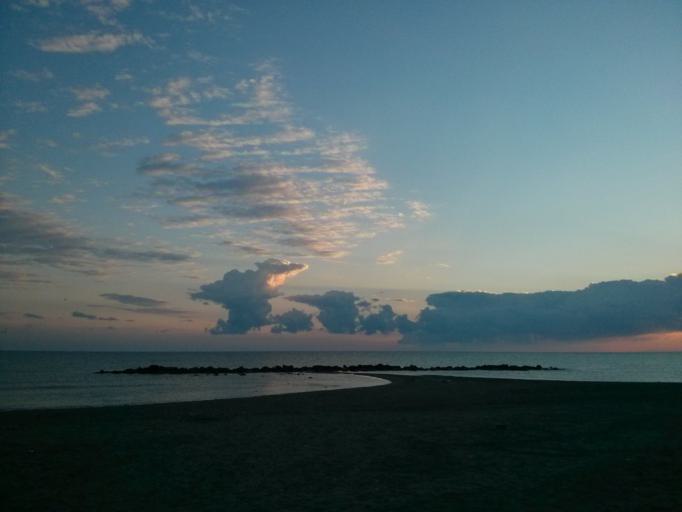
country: TR
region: Sakarya
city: Karasu
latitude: 41.1143
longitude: 30.6831
